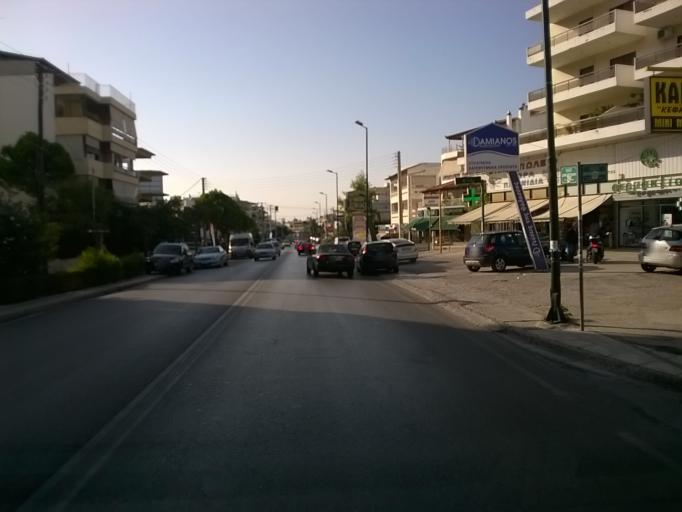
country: GR
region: Attica
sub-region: Nomarchia Athinas
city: Glyfada
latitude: 37.8753
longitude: 23.7639
